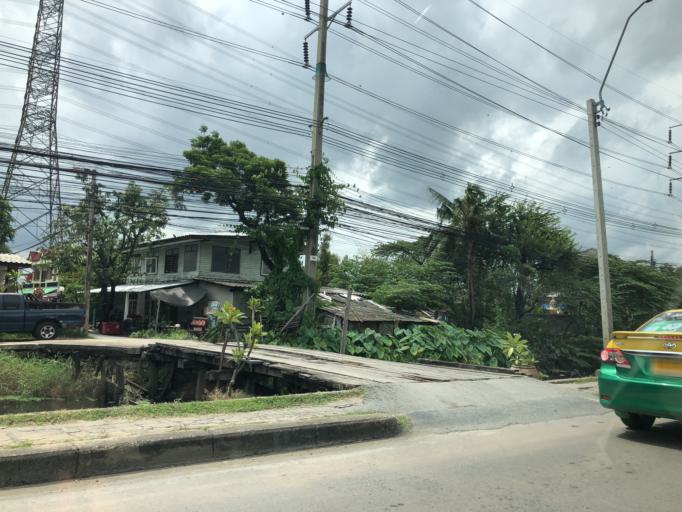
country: TH
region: Bangkok
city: Lak Si
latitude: 13.8830
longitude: 100.5514
